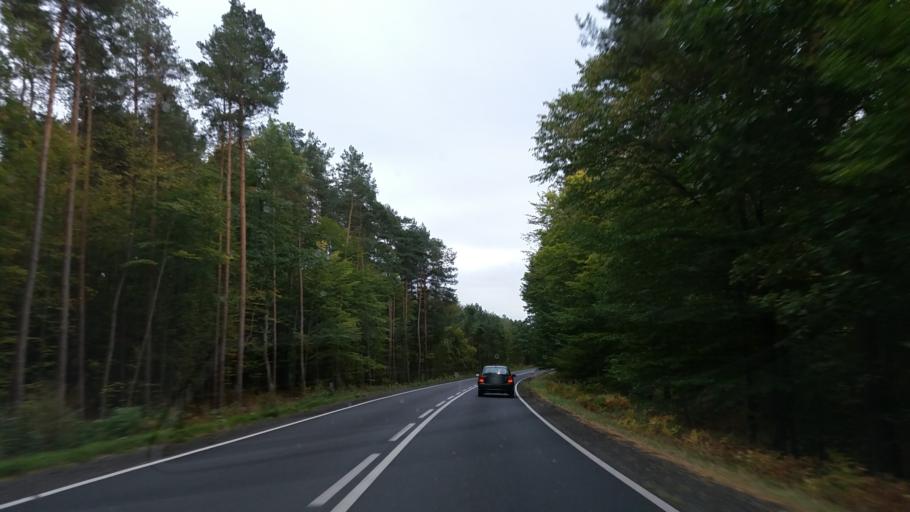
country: PL
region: Lubusz
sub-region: Powiat gorzowski
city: Klodawa
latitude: 52.8743
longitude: 15.2018
